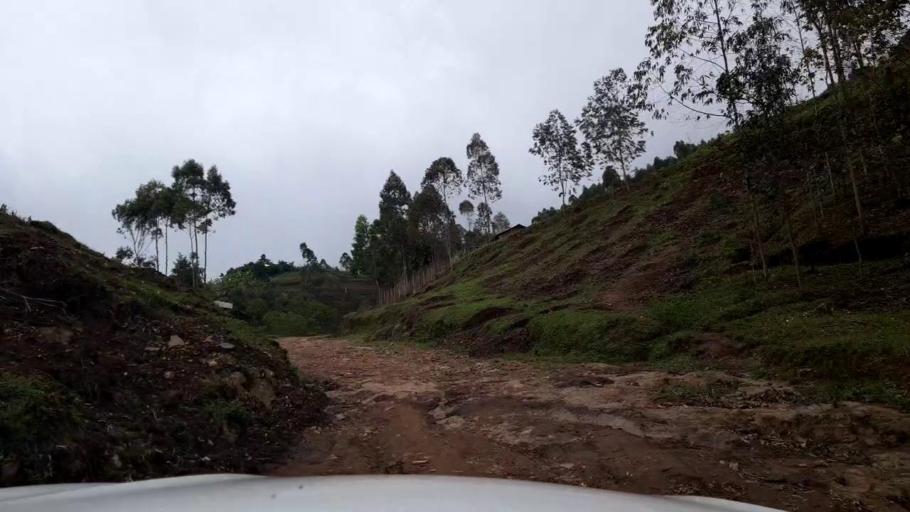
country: RW
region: Northern Province
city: Musanze
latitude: -1.6091
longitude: 29.7674
